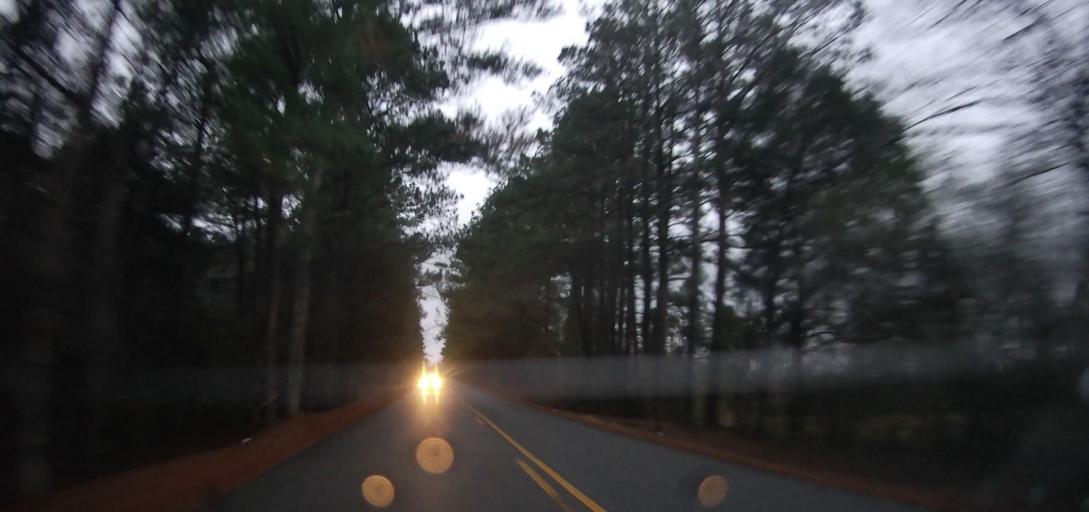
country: US
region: Alabama
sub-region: Tuscaloosa County
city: Vance
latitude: 33.1385
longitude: -87.2297
